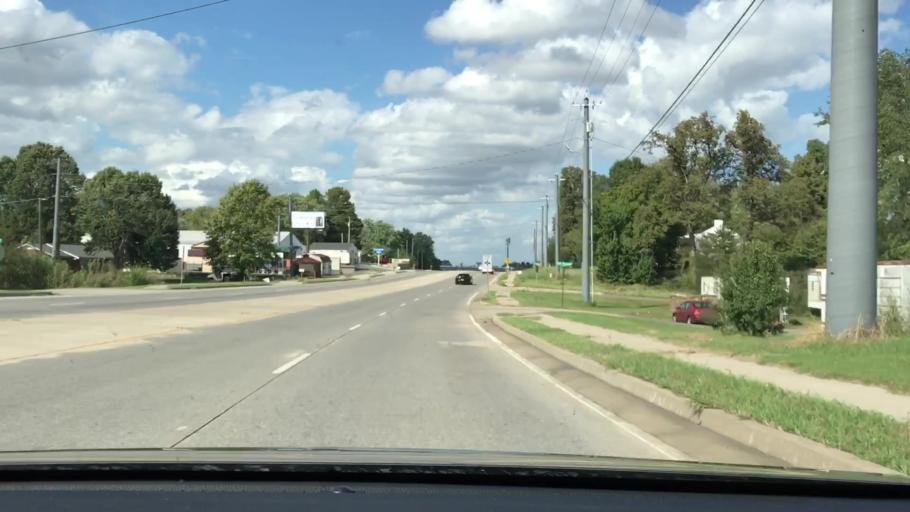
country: US
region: Kentucky
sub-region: Graves County
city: Mayfield
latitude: 36.7622
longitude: -88.6426
